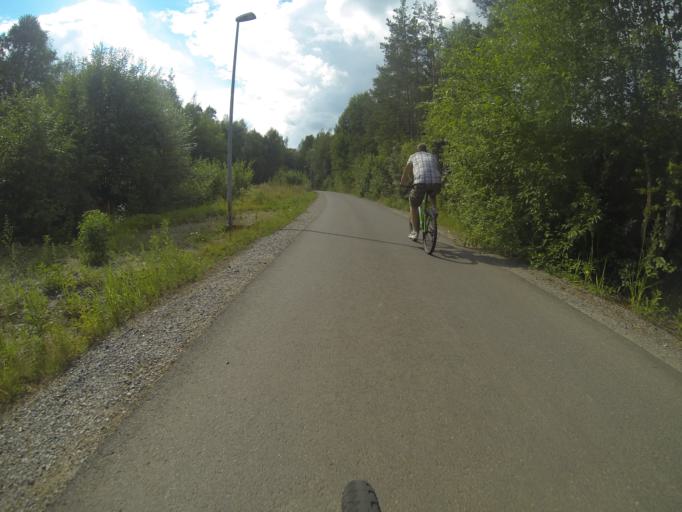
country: FI
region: Southern Savonia
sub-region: Savonlinna
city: Savonlinna
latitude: 61.8796
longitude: 28.8687
